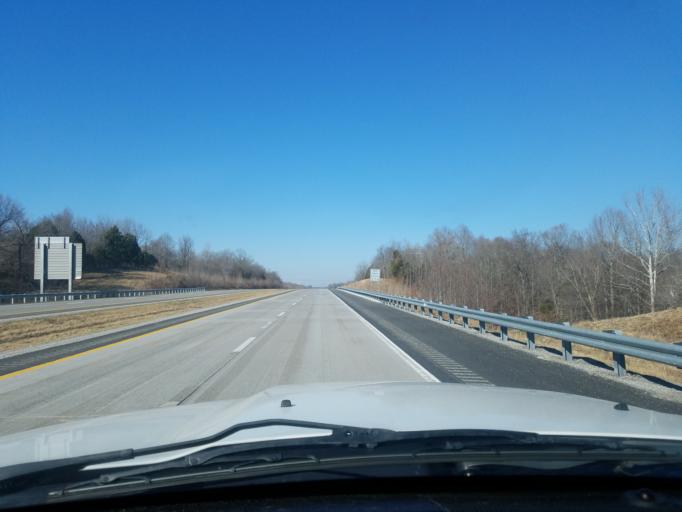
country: US
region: Kentucky
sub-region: Ohio County
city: Beaver Dam
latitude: 37.3961
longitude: -86.8168
